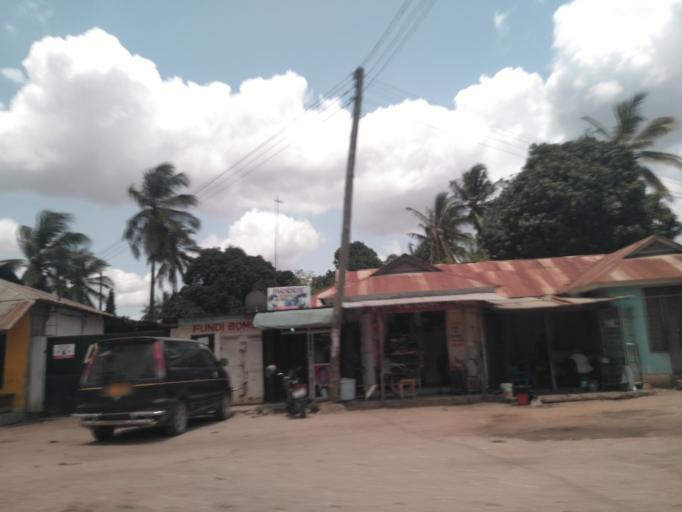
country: TZ
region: Dar es Salaam
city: Dar es Salaam
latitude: -6.8538
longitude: 39.3549
